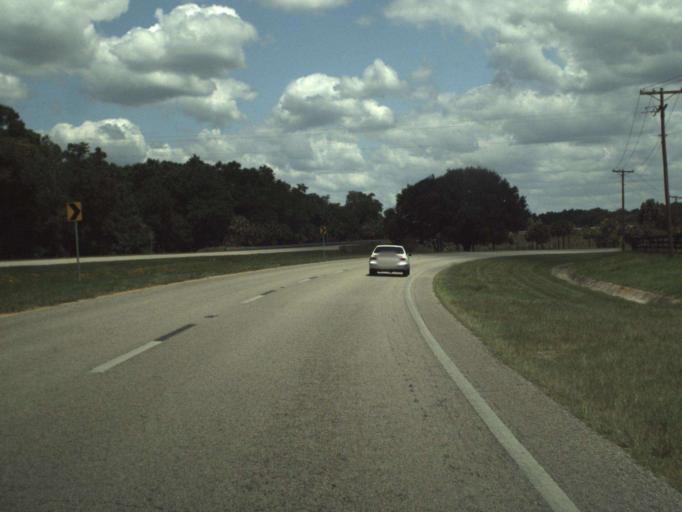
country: US
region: Florida
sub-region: Marion County
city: Citra
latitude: 29.3453
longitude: -82.1536
